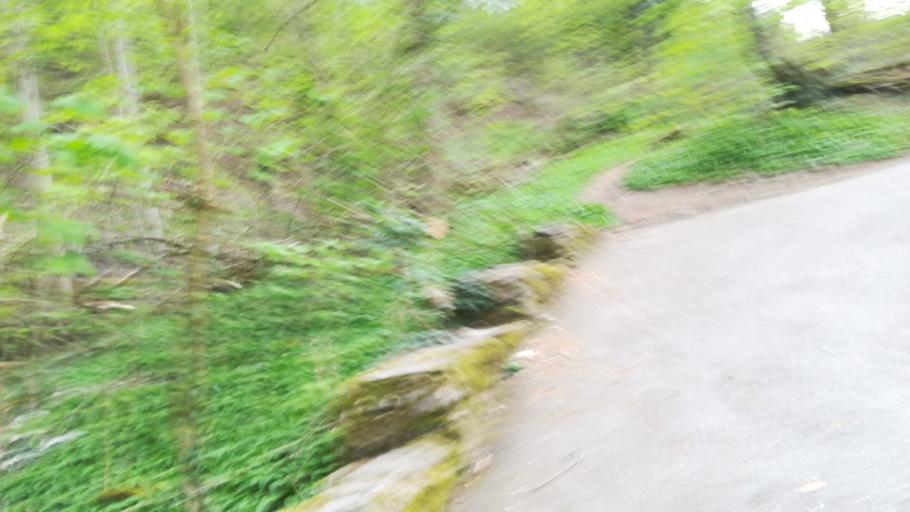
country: DE
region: Baden-Wuerttemberg
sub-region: Freiburg Region
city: Singen
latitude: 47.7661
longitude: 8.8177
